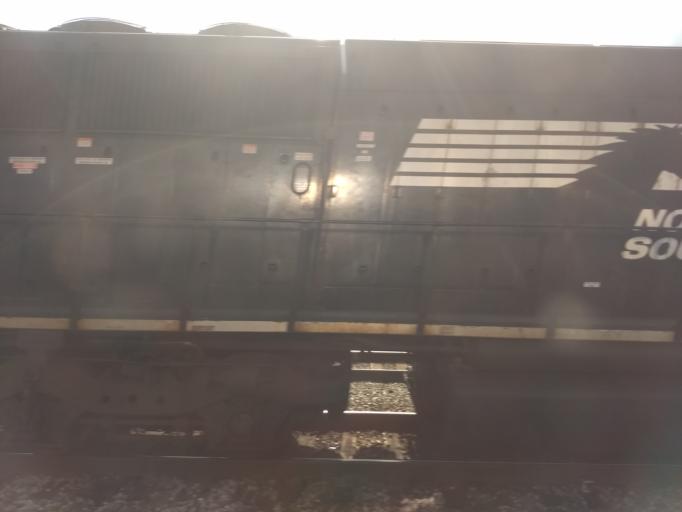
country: US
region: Pennsylvania
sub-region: Blair County
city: Altoona
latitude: 40.5330
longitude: -78.3823
